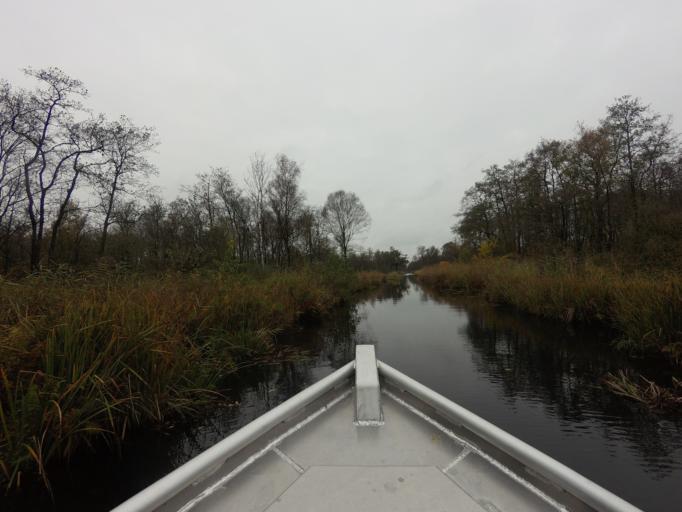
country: NL
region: Overijssel
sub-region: Gemeente Steenwijkerland
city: Oldemarkt
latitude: 52.7859
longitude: 5.9505
